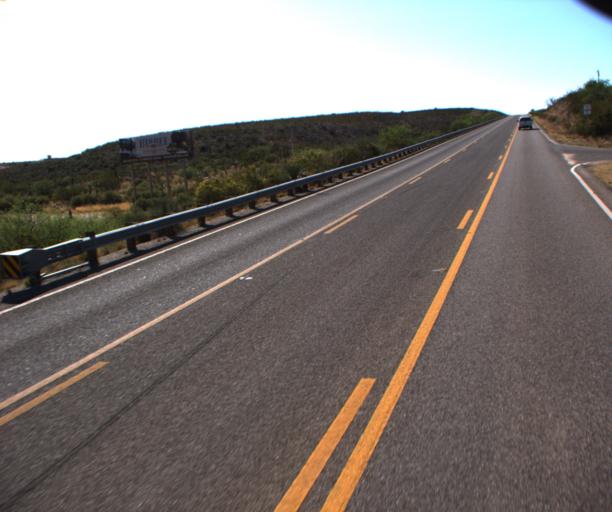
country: US
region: Arizona
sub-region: Cochise County
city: Tombstone
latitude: 31.7302
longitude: -110.0791
